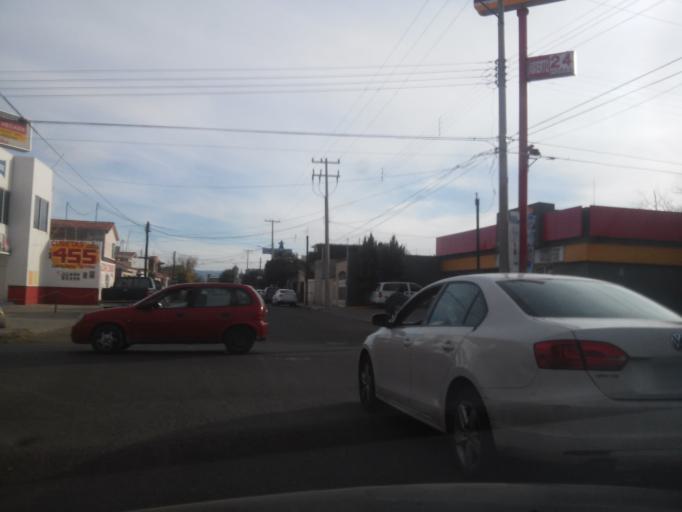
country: MX
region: Durango
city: Victoria de Durango
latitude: 24.0249
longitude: -104.6540
